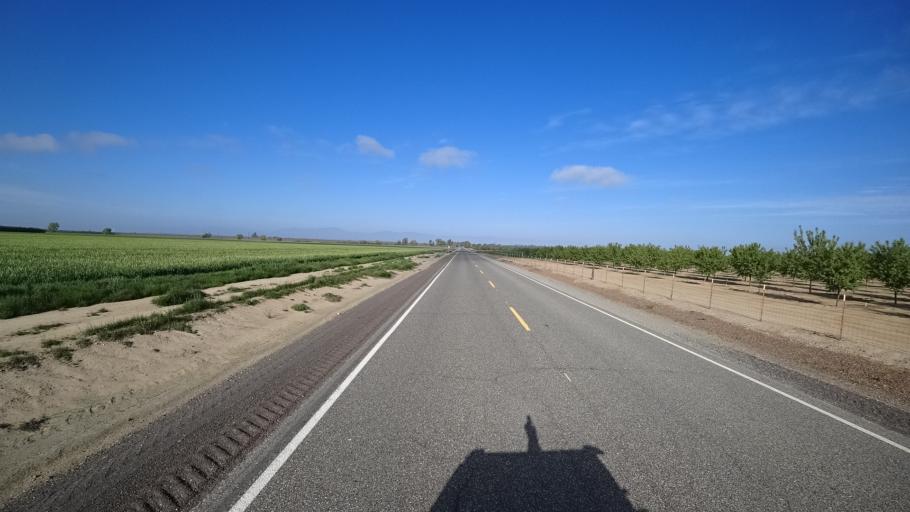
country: US
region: California
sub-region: Glenn County
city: Willows
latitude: 39.5823
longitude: -122.1663
